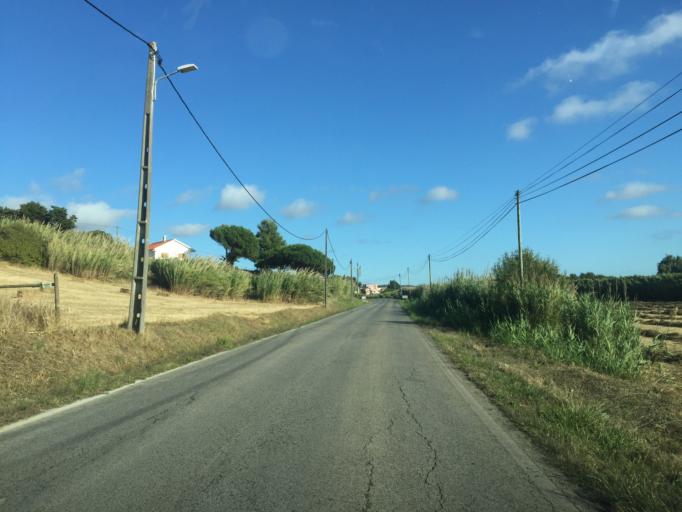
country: PT
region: Lisbon
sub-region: Torres Vedras
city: A dos Cunhados
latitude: 39.1593
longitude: -9.3034
